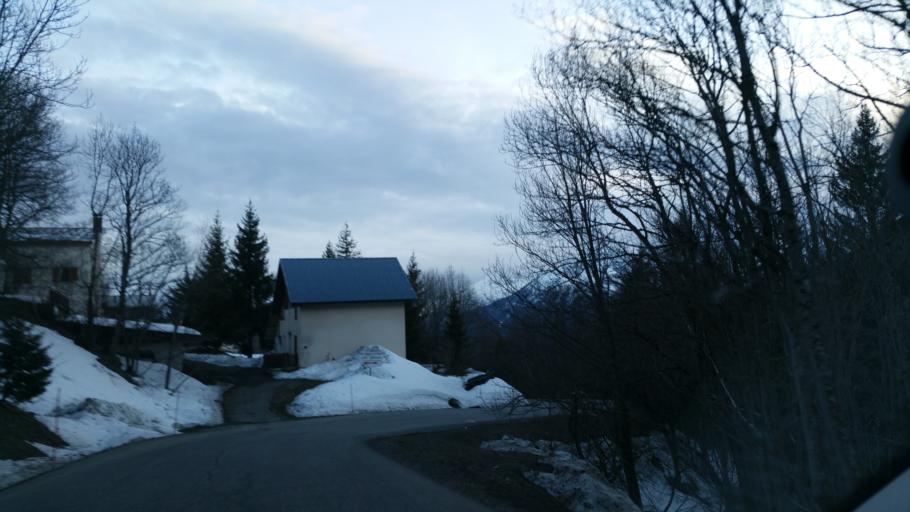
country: FR
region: Rhone-Alpes
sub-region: Departement de la Savoie
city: La Chambre
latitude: 45.4129
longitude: 6.3497
